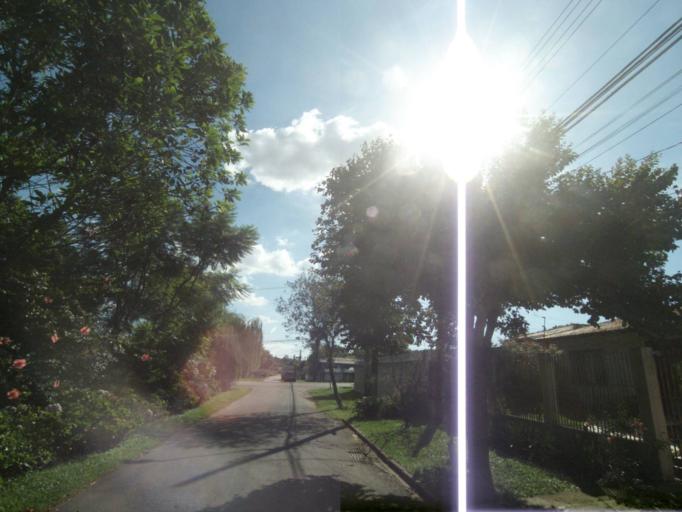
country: BR
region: Parana
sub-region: Pinhais
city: Pinhais
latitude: -25.4558
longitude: -49.2081
